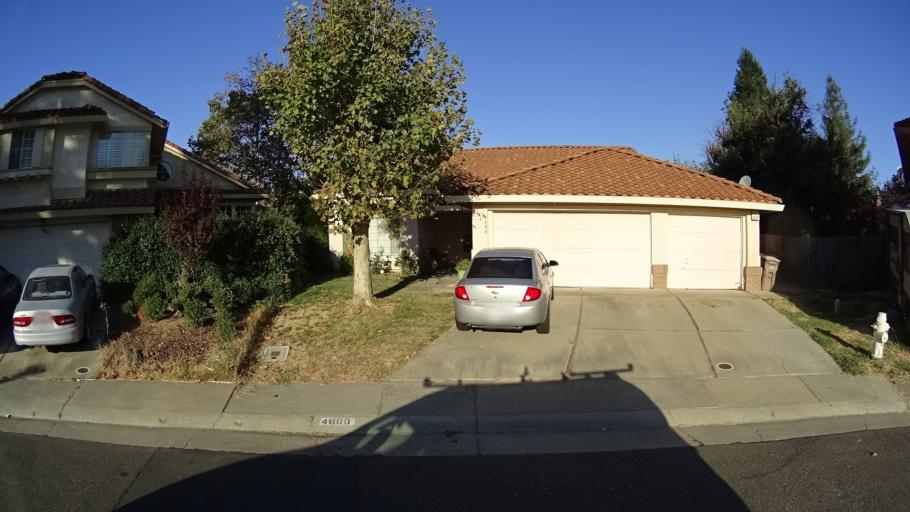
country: US
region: California
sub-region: Sacramento County
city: Laguna
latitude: 38.4260
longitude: -121.4519
